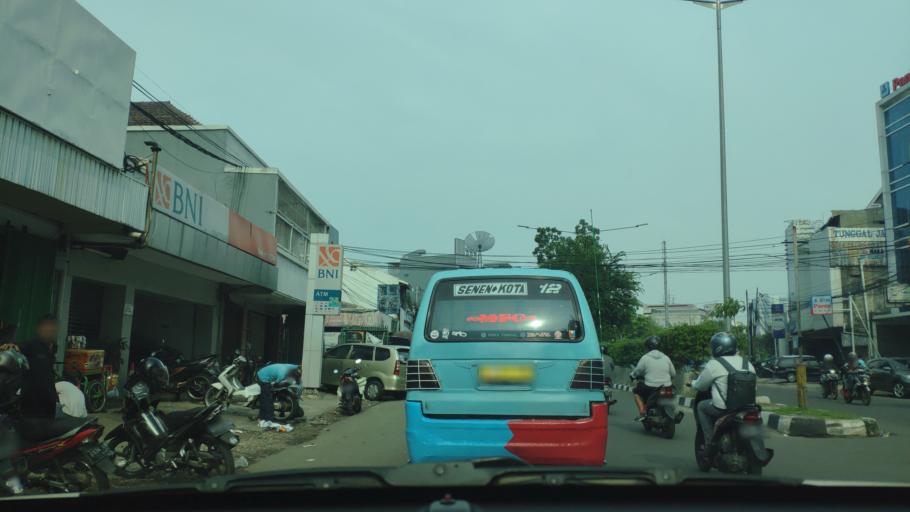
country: ID
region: Jakarta Raya
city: Jakarta
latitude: -6.1595
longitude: 106.8200
